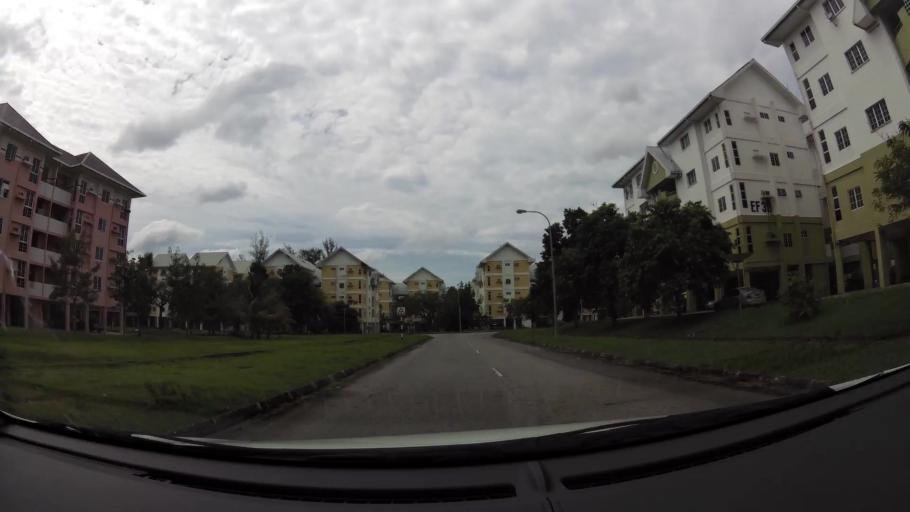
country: BN
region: Brunei and Muara
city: Bandar Seri Begawan
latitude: 4.9023
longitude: 114.9082
